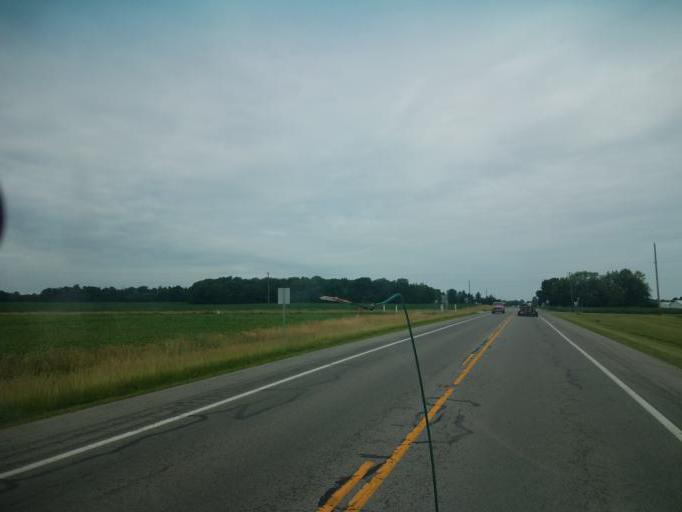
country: US
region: Ohio
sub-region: Hardin County
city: Ada
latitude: 40.7261
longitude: -83.7837
